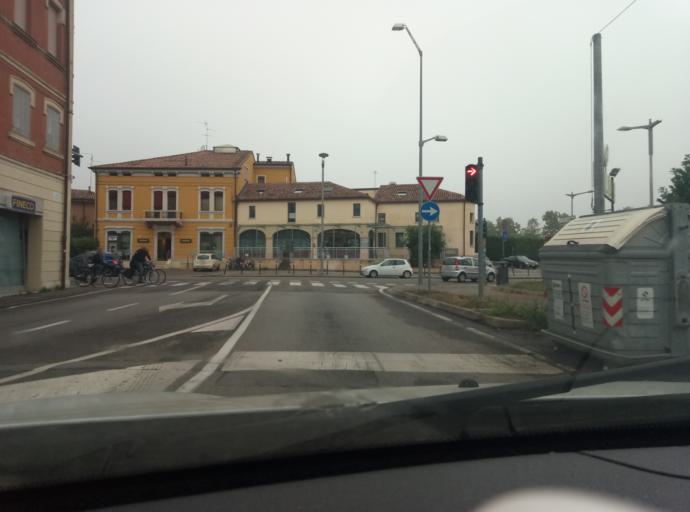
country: IT
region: Emilia-Romagna
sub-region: Provincia di Ferrara
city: Ferrara
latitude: 44.8307
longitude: 11.6155
